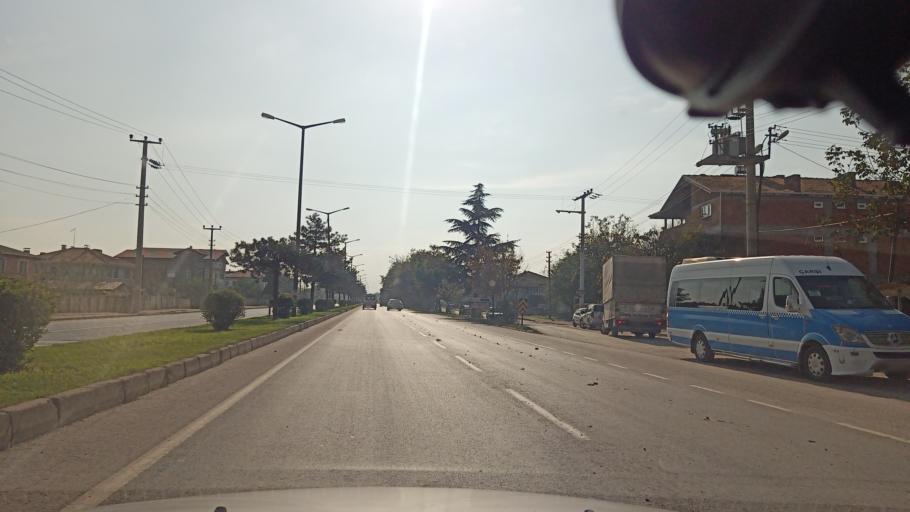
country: TR
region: Sakarya
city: Adapazari
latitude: 40.8093
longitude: 30.4053
